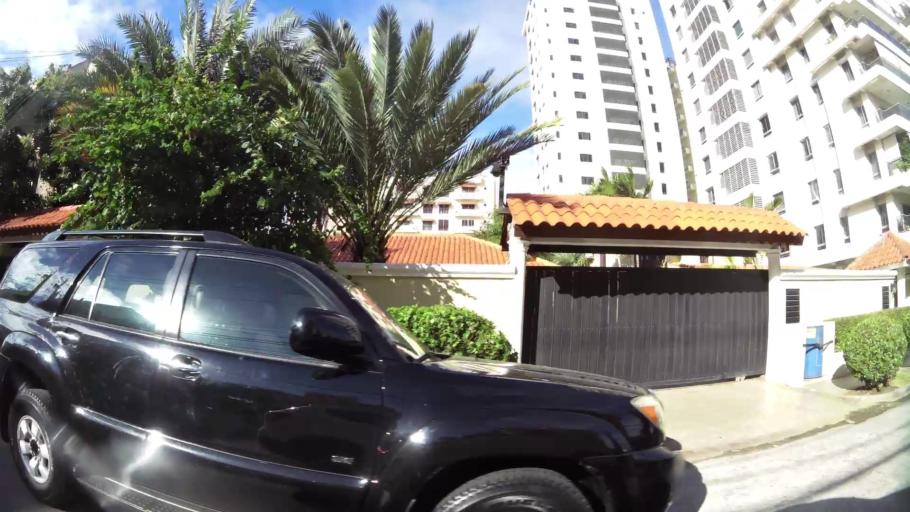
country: DO
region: Nacional
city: La Julia
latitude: 18.4742
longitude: -69.9377
